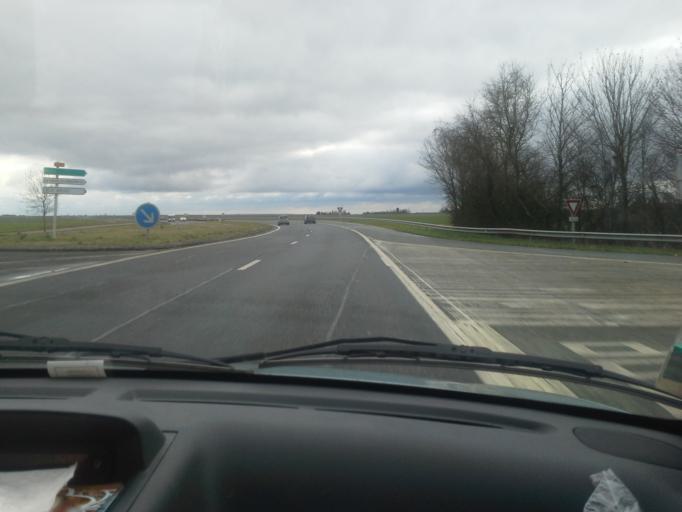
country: FR
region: Centre
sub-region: Departement du Loir-et-Cher
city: Herbault
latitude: 47.7208
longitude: 1.1535
